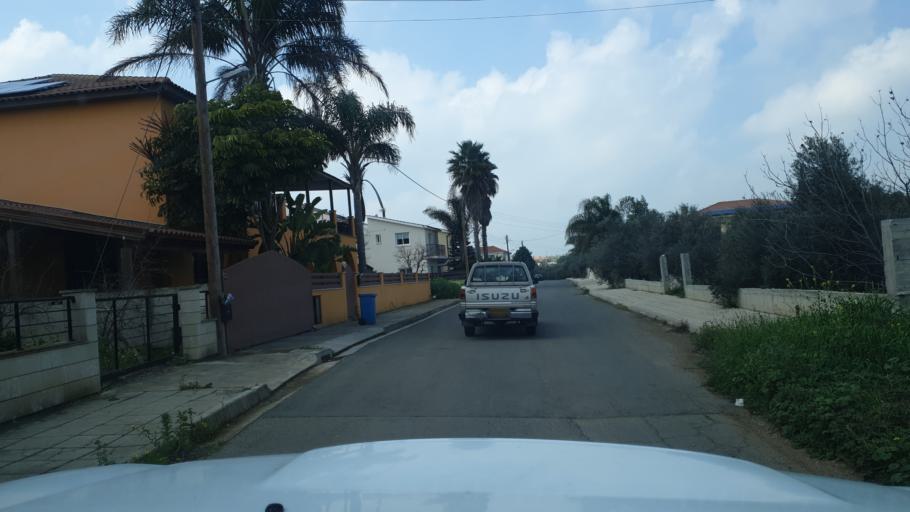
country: CY
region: Lefkosia
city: Kato Deftera
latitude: 35.0879
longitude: 33.2896
